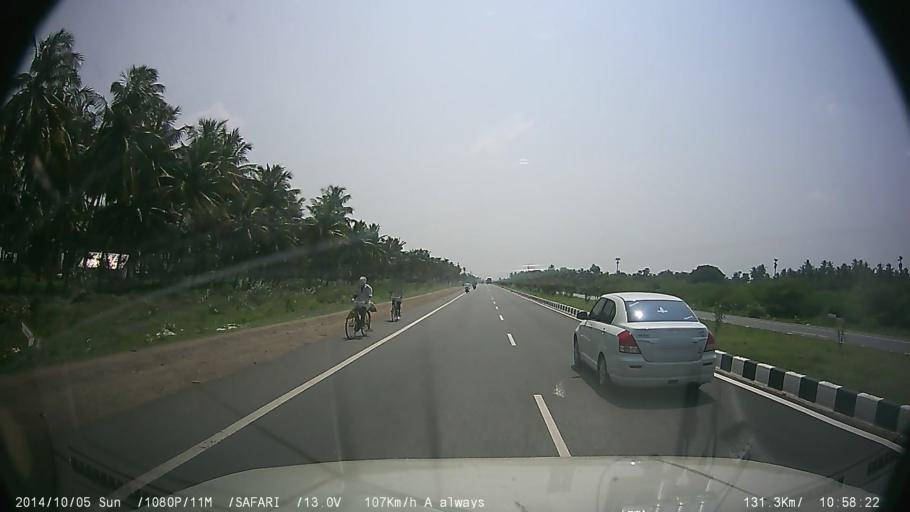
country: IN
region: Tamil Nadu
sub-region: Salem
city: Attur
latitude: 11.6447
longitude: 78.5151
